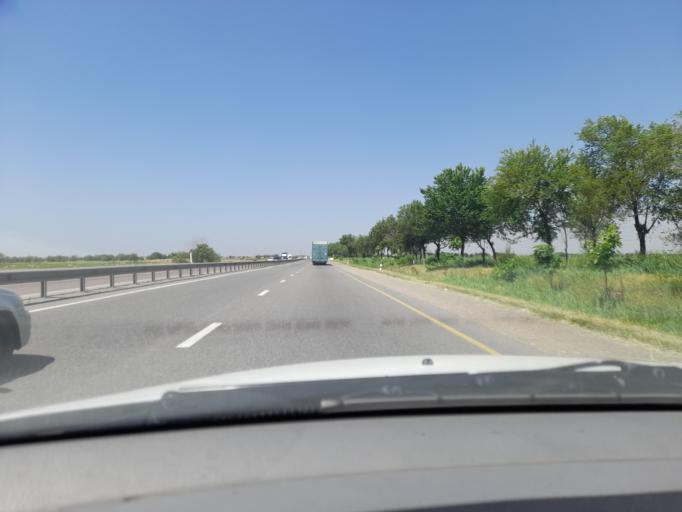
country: KZ
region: Ongtustik Qazaqstan
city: Myrzakent
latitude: 40.5292
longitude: 68.4420
